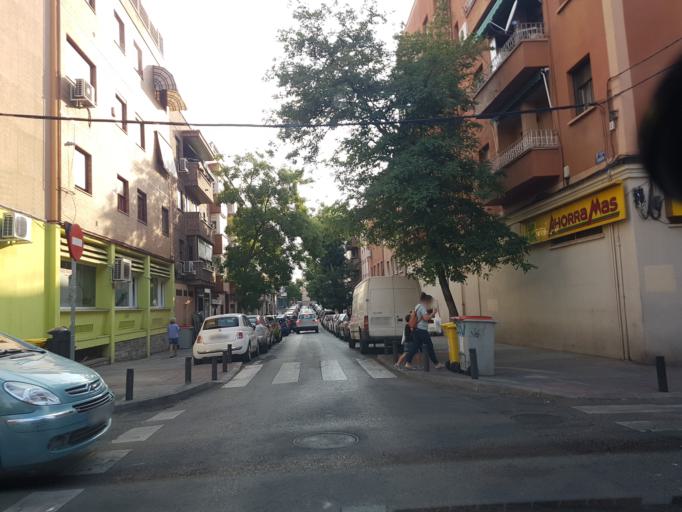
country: ES
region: Madrid
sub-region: Provincia de Madrid
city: Ciudad Lineal
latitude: 40.4371
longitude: -3.6439
